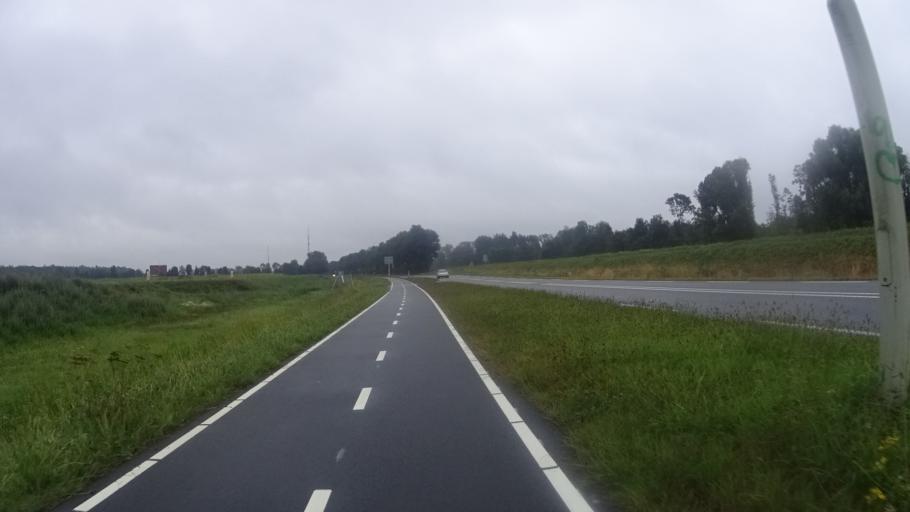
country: NL
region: Groningen
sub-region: Gemeente  Oldambt
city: Winschoten
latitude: 53.1644
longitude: 7.0002
